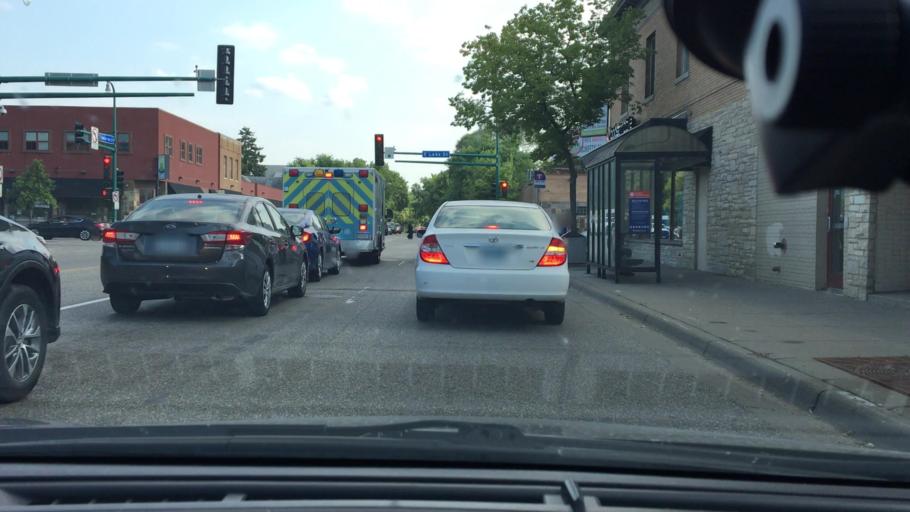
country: US
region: Minnesota
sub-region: Hennepin County
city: Minneapolis
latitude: 44.9488
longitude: -93.2475
